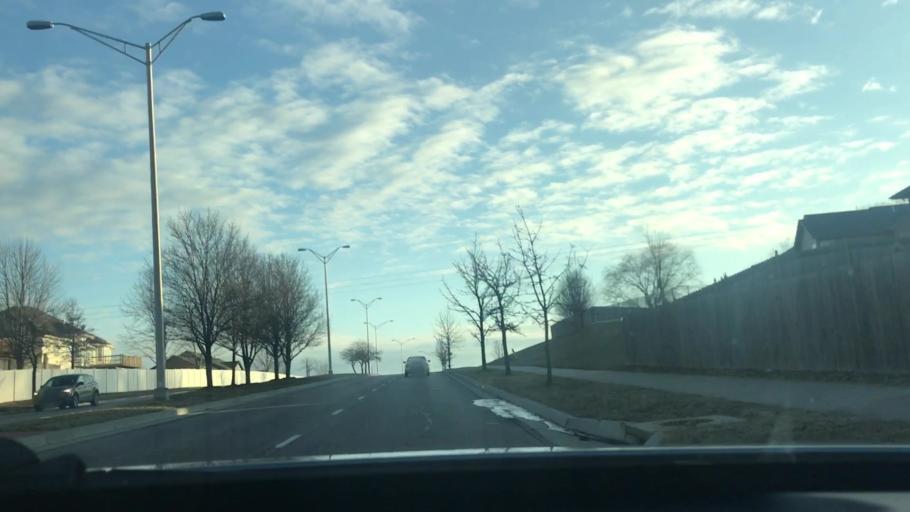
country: US
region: Missouri
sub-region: Jackson County
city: Lees Summit
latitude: 38.9372
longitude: -94.3438
